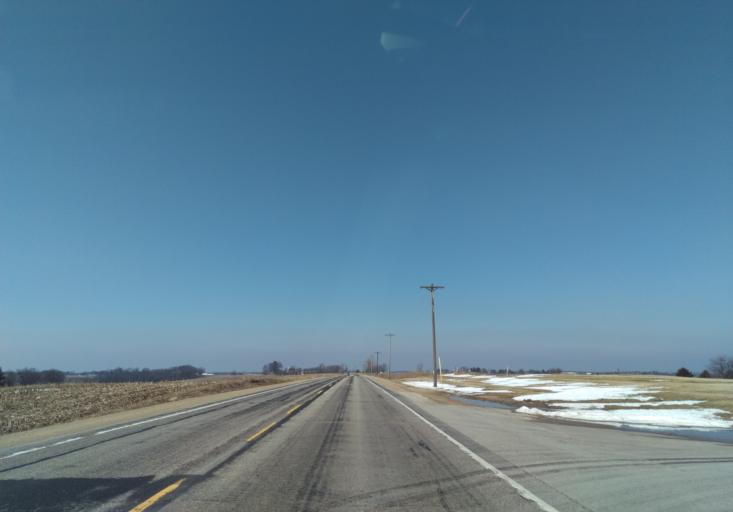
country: US
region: Wisconsin
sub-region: Vernon County
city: Westby
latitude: 43.6632
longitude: -90.8644
